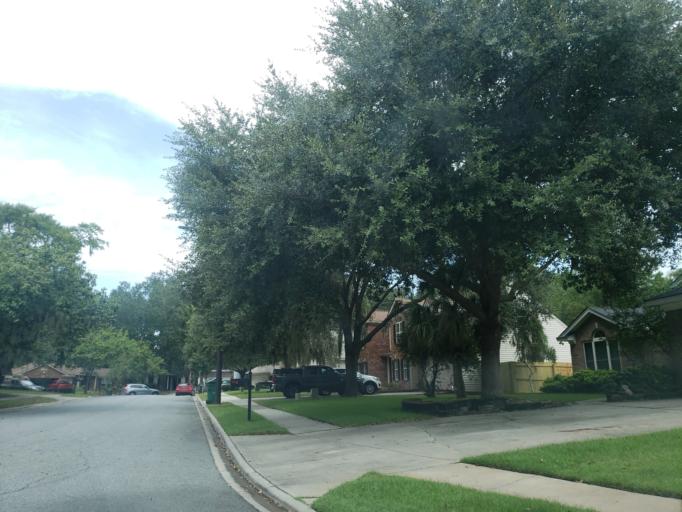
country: US
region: Georgia
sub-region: Chatham County
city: Wilmington Island
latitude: 31.9978
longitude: -80.9754
